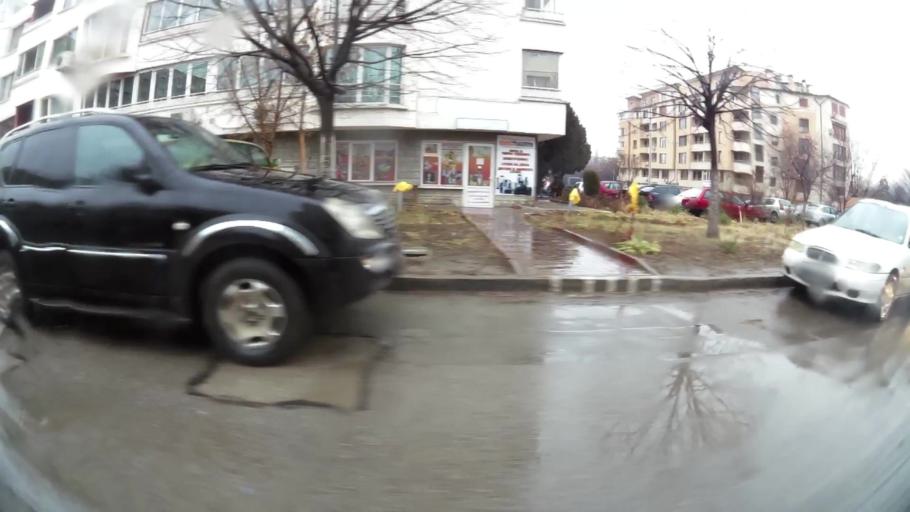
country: BG
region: Sofia-Capital
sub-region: Stolichna Obshtina
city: Sofia
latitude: 42.6602
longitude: 23.3660
